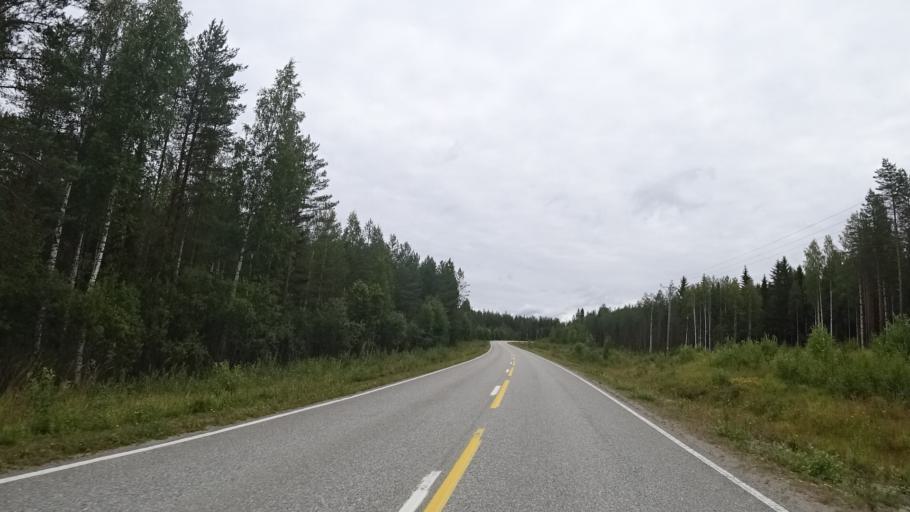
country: FI
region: North Karelia
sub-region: Joensuu
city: Ilomantsi
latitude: 62.6220
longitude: 31.2363
